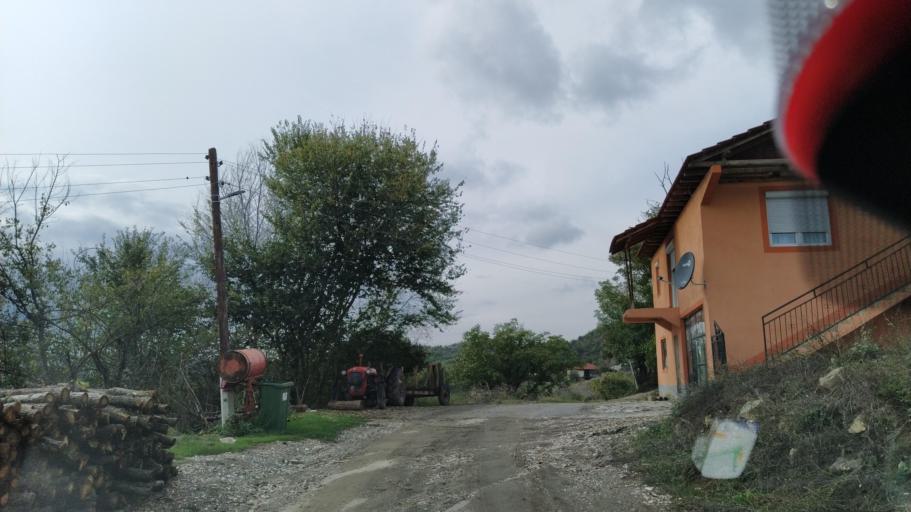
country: MK
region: Strumica
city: Veljusa
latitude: 41.5122
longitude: 22.4922
